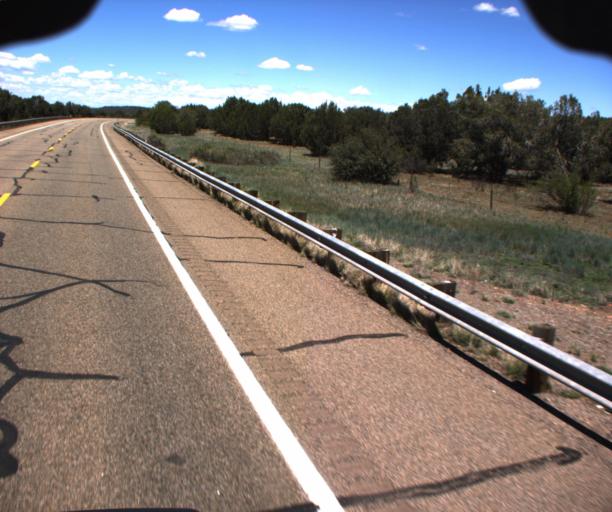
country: US
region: Arizona
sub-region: Yavapai County
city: Paulden
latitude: 35.1053
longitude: -112.4279
